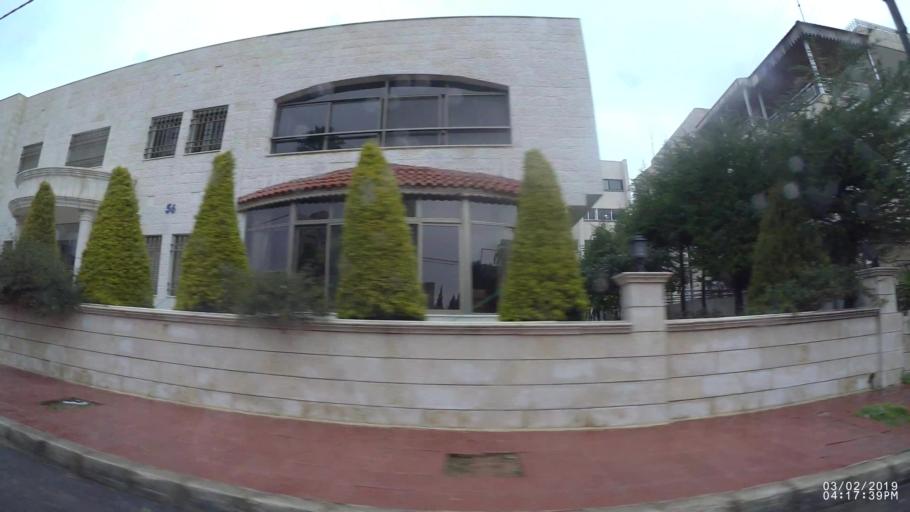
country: JO
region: Amman
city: Amman
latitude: 31.9680
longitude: 35.9127
